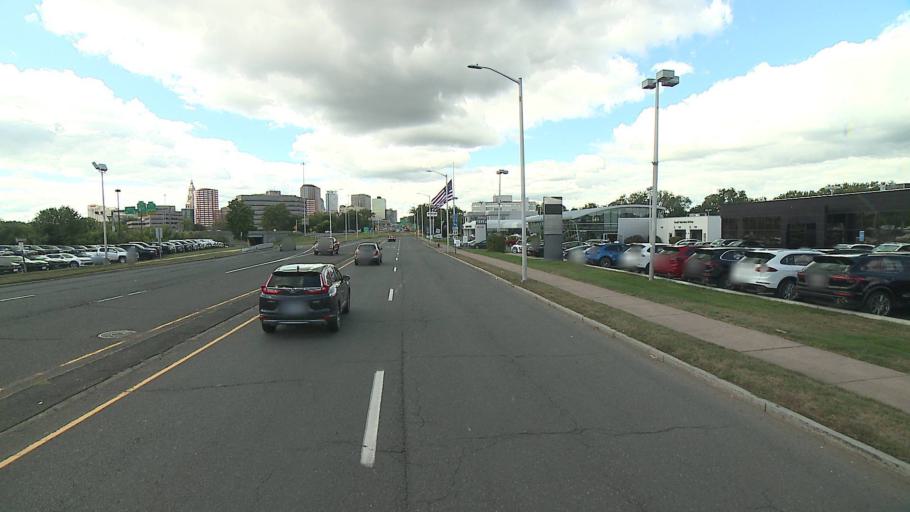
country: US
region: Connecticut
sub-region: Hartford County
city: Hartford
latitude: 41.7696
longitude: -72.6579
